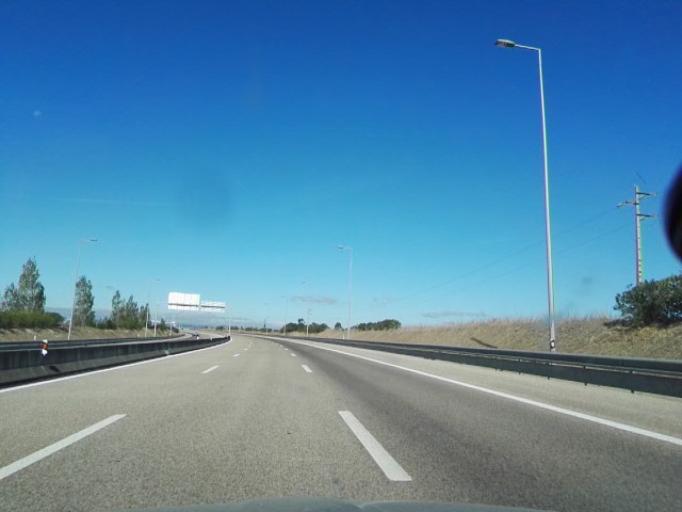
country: PT
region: Santarem
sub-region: Benavente
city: Benavente
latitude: 38.9651
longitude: -8.8394
